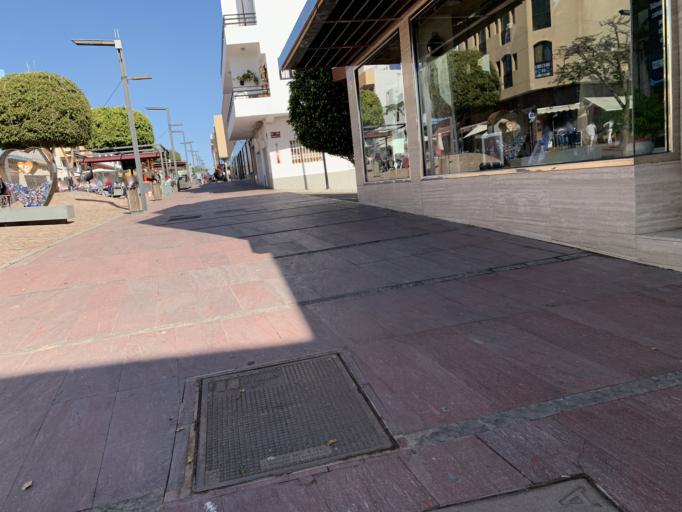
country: ES
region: Canary Islands
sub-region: Provincia de Las Palmas
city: Puerto del Rosario
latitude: 28.4964
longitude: -13.8612
